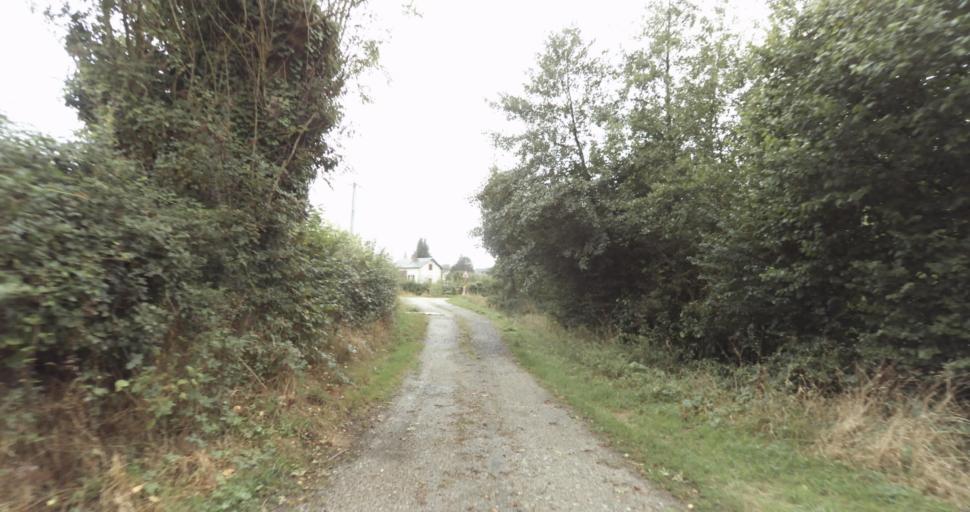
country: FR
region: Lower Normandy
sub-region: Departement de l'Orne
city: Sainte-Gauburge-Sainte-Colombe
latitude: 48.7185
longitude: 0.4320
